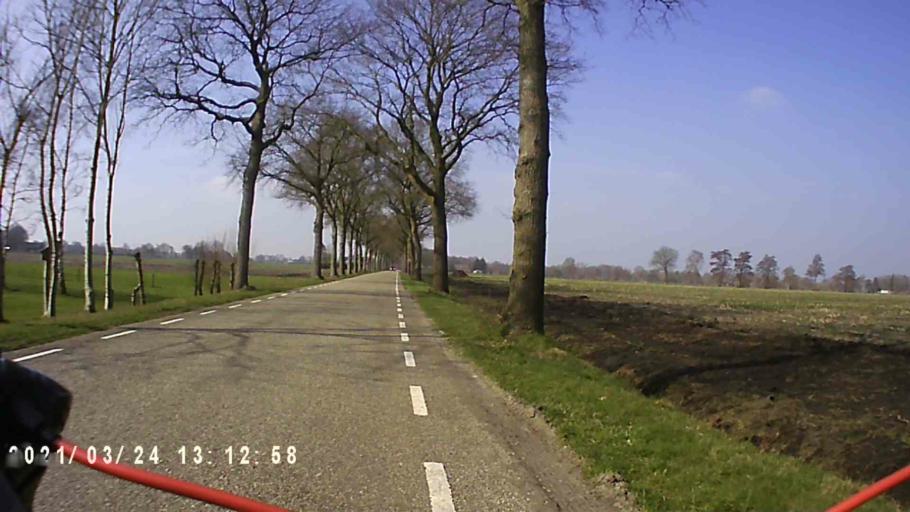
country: NL
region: Groningen
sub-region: Gemeente Leek
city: Leek
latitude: 53.1199
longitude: 6.2948
